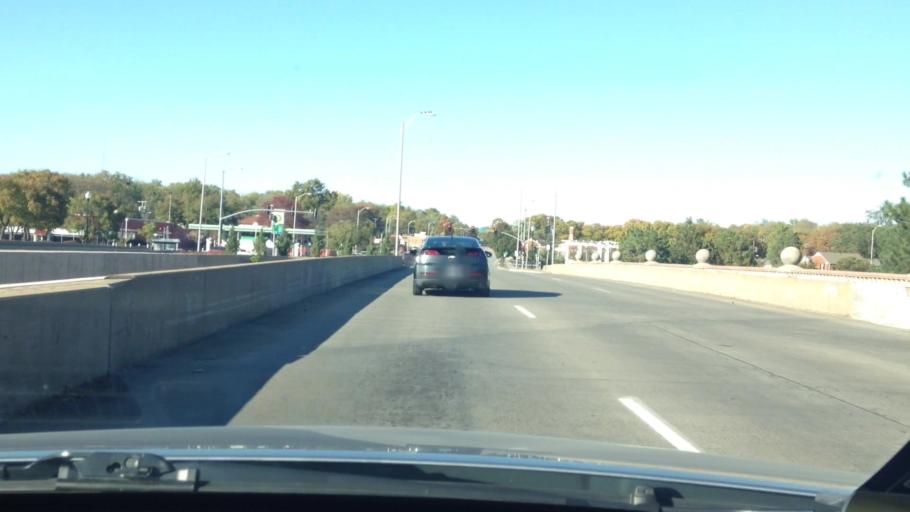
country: US
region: Kansas
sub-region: Johnson County
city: Westwood
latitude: 39.0403
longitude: -94.5682
